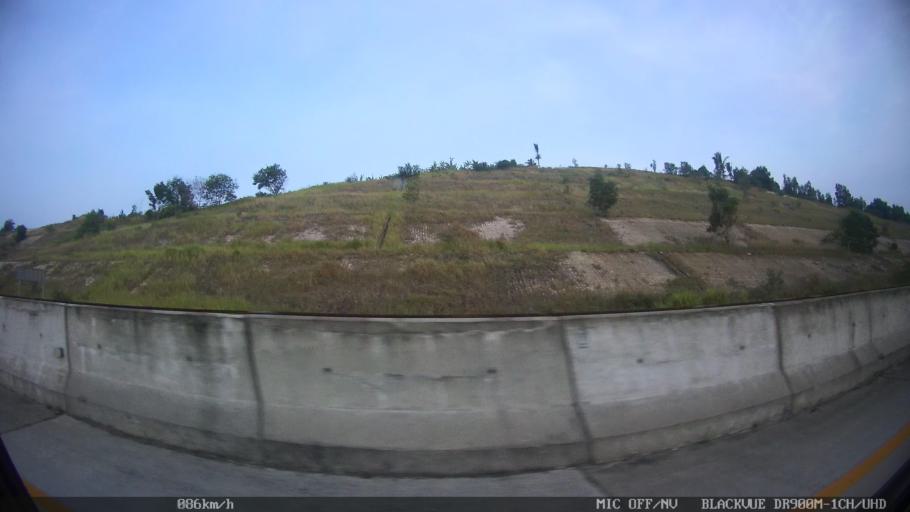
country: ID
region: Lampung
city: Penengahan
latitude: -5.8264
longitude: 105.7339
